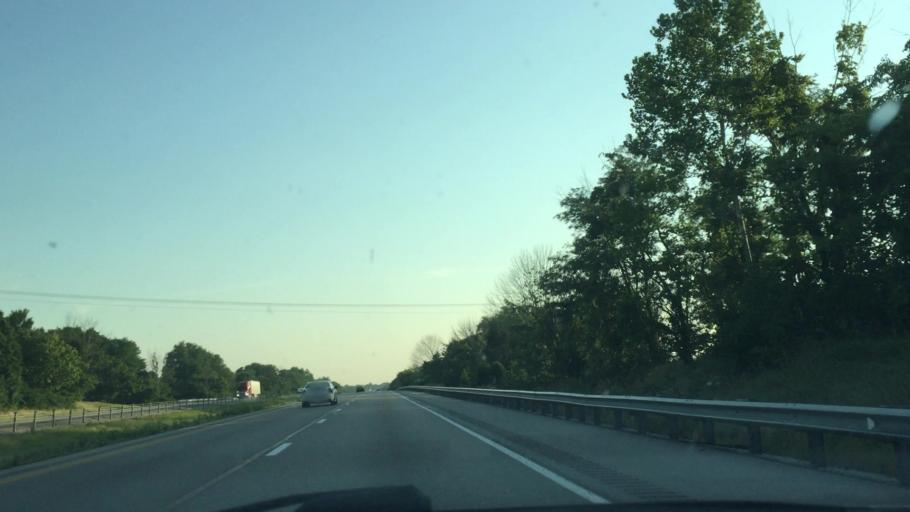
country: US
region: Kentucky
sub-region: Boone County
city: Verona
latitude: 38.7750
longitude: -84.7720
